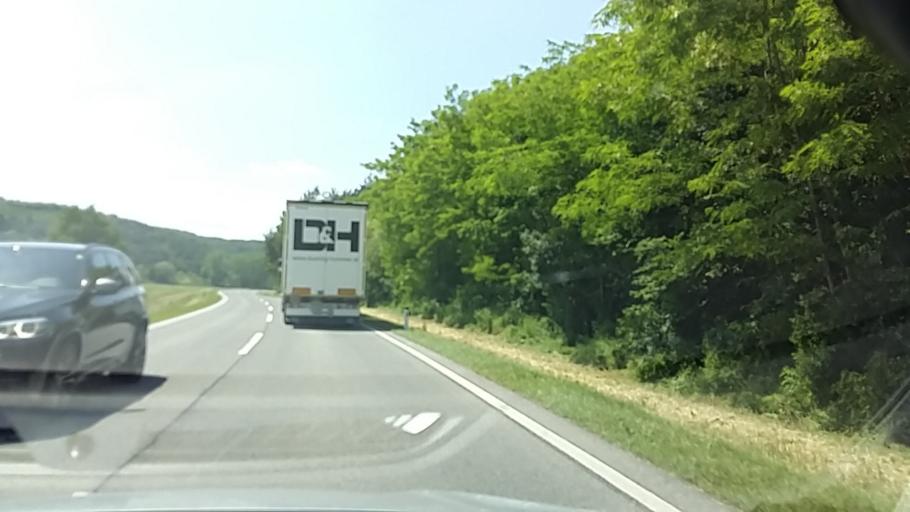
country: AT
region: Burgenland
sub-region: Politischer Bezirk Oberpullendorf
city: Piringsdorf
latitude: 47.4638
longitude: 16.4490
